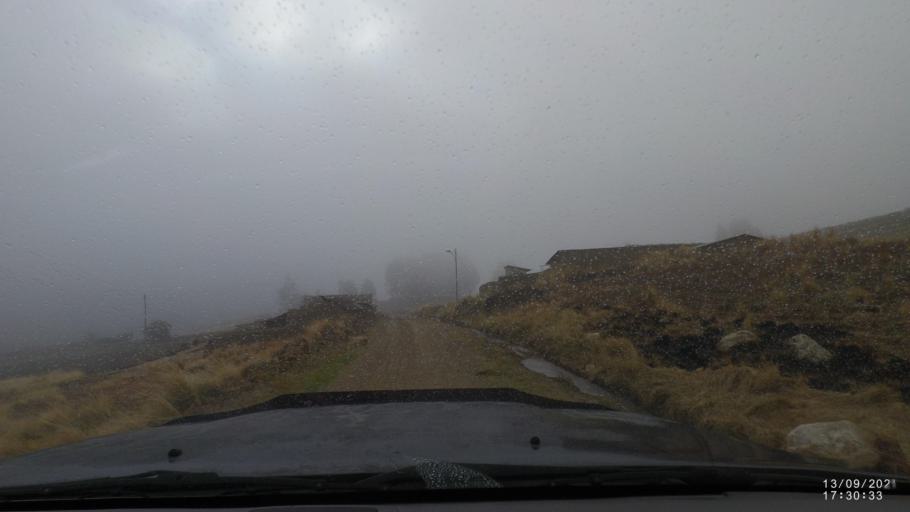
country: BO
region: Cochabamba
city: Colomi
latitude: -17.3612
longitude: -65.7873
